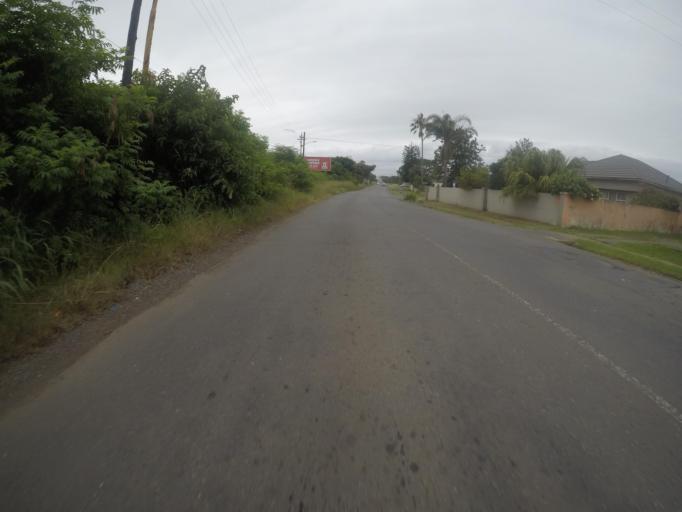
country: ZA
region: Eastern Cape
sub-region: Buffalo City Metropolitan Municipality
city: East London
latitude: -32.9723
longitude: 27.8832
